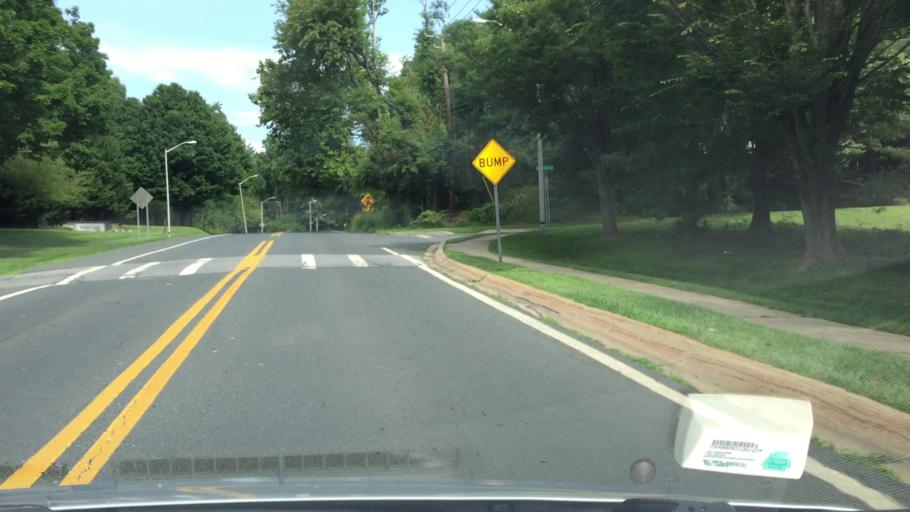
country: US
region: Maryland
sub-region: Montgomery County
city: Potomac
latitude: 39.0215
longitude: -77.1816
